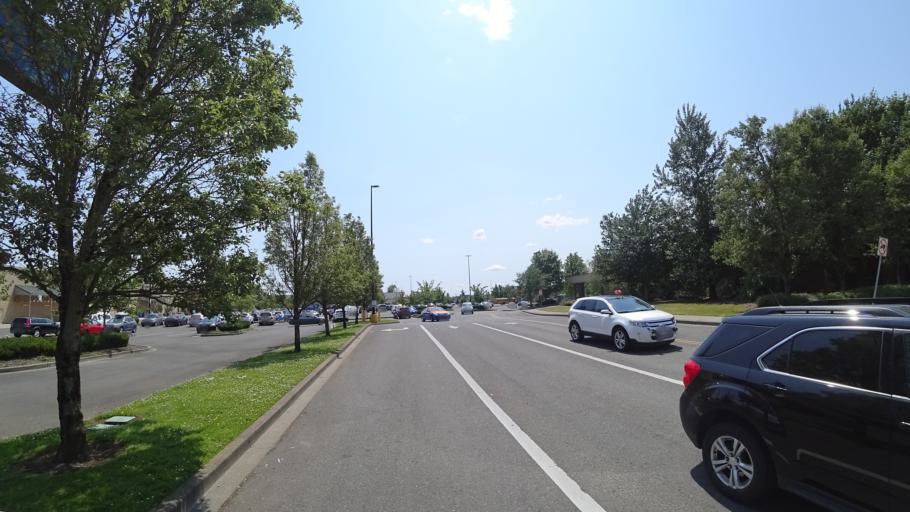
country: US
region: Oregon
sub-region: Multnomah County
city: Lents
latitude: 45.4513
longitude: -122.5766
